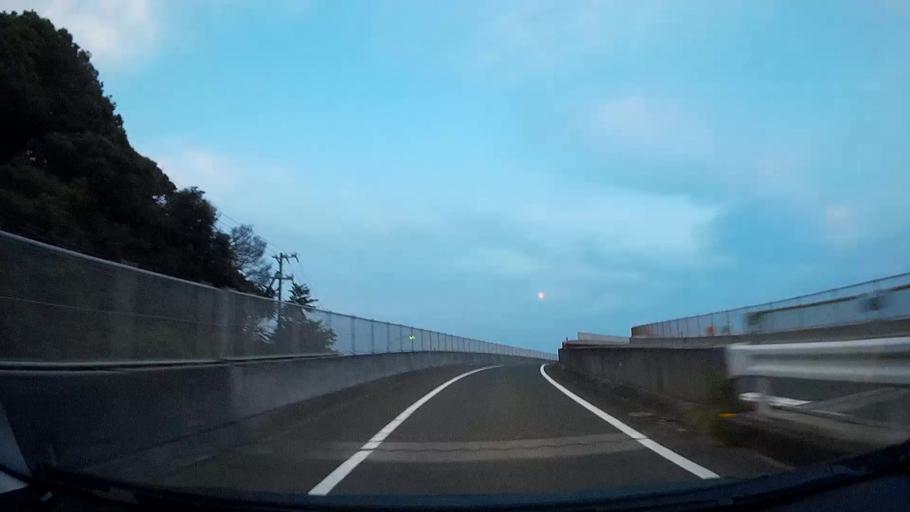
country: JP
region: Shizuoka
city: Kosai-shi
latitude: 34.6798
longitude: 137.5110
